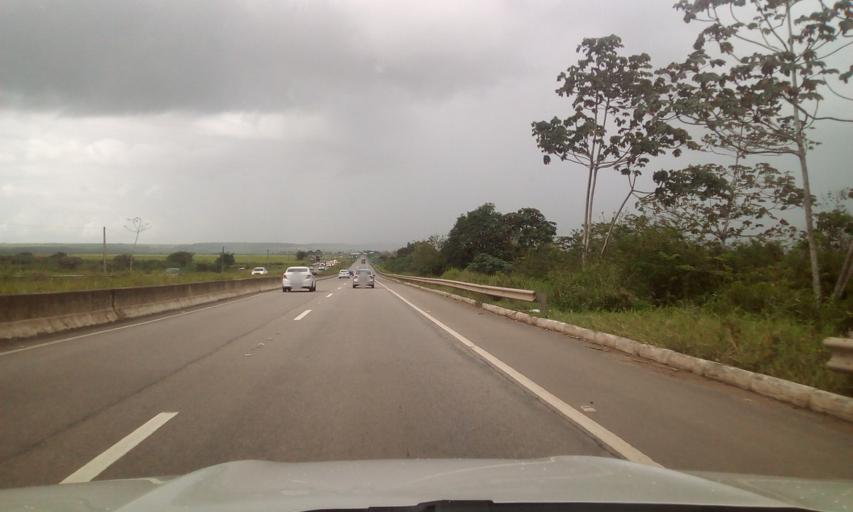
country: BR
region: Pernambuco
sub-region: Goiana
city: Goiana
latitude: -7.5362
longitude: -34.9915
